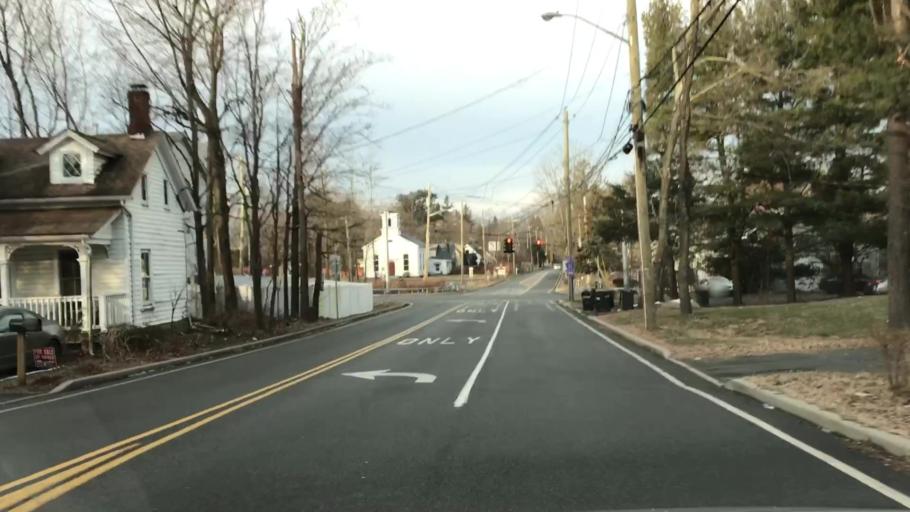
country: US
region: New York
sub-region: Rockland County
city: Viola
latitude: 41.1364
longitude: -74.0822
